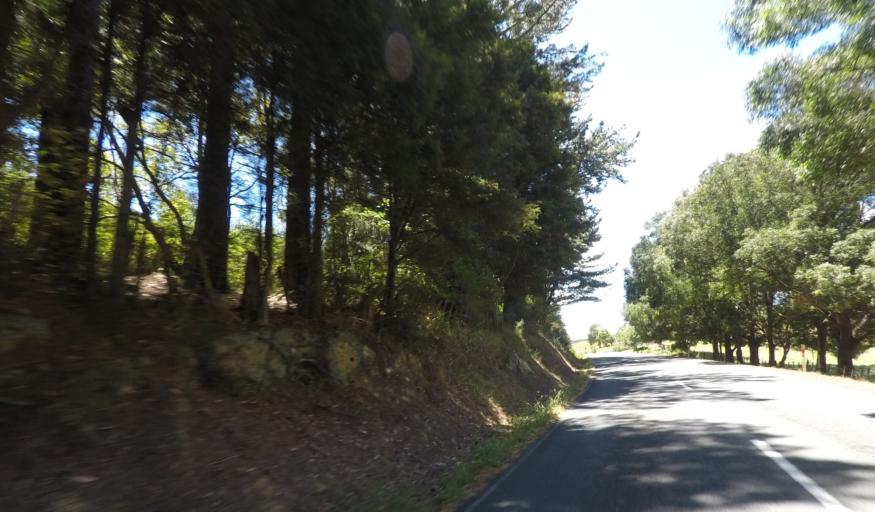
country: NZ
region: Northland
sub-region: Whangarei
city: Whangarei
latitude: -35.5452
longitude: 174.3059
